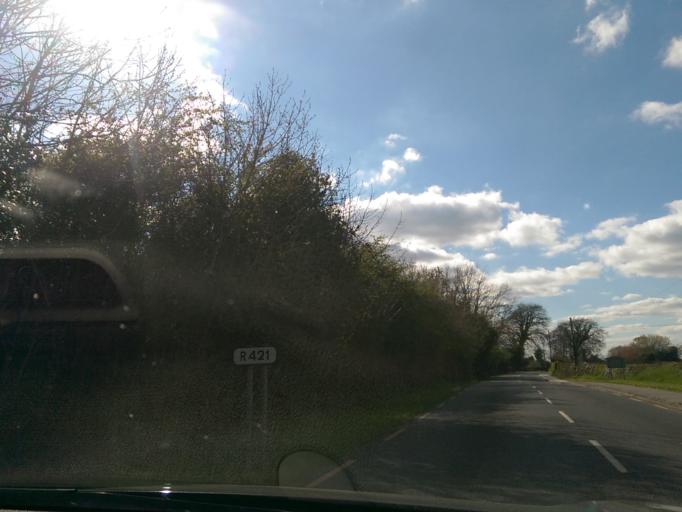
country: IE
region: Munster
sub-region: North Tipperary
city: Roscrea
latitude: 53.0985
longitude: -7.7266
